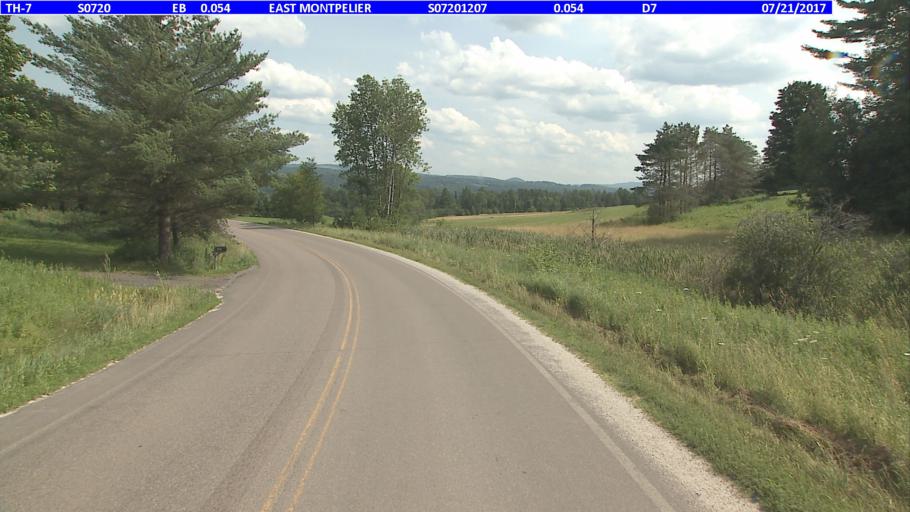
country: US
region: Vermont
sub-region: Washington County
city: Montpelier
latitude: 44.2772
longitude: -72.4985
